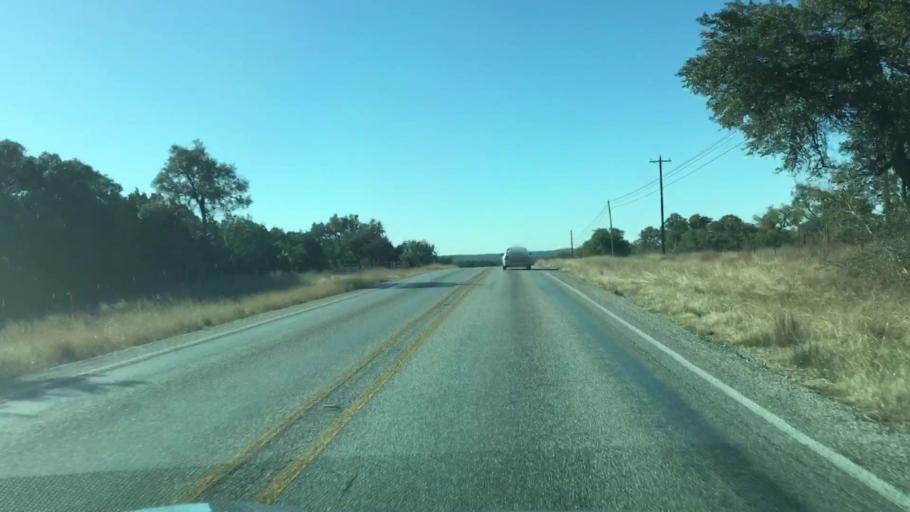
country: US
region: Texas
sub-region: Blanco County
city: Blanco
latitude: 30.1050
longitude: -98.3463
